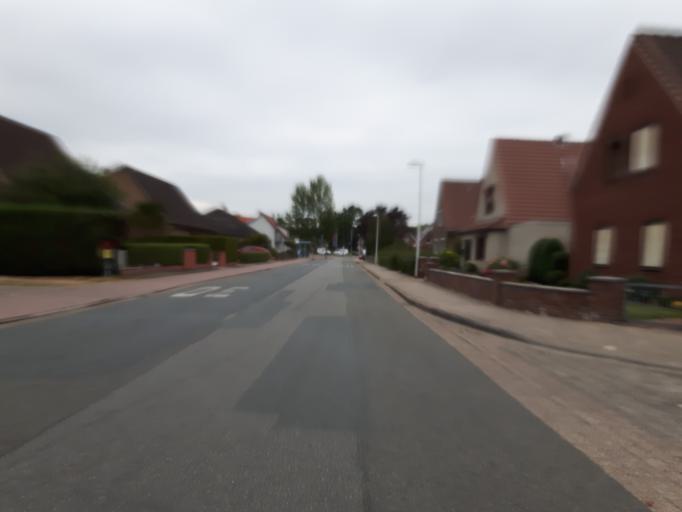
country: DE
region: Lower Saxony
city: Delmenhorst
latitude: 53.0246
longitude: 8.6532
